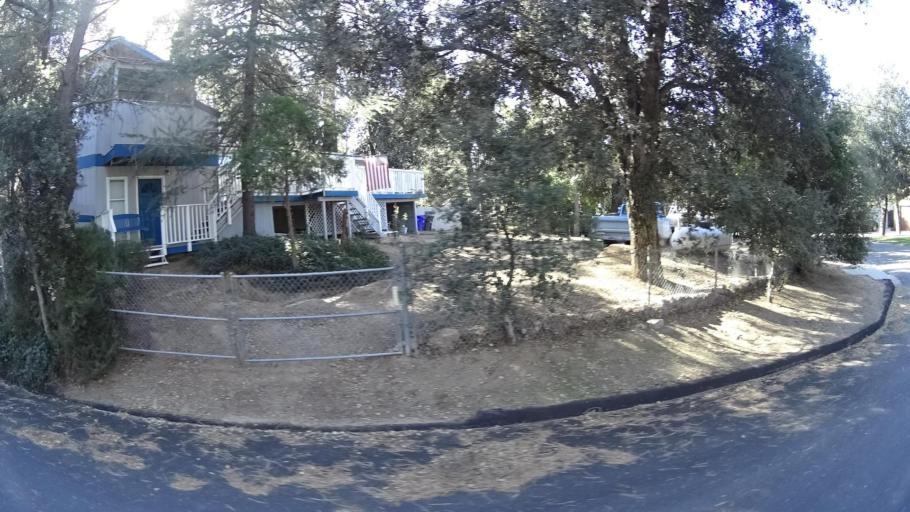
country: US
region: California
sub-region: San Diego County
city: Pine Valley
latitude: 32.8350
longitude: -116.5273
